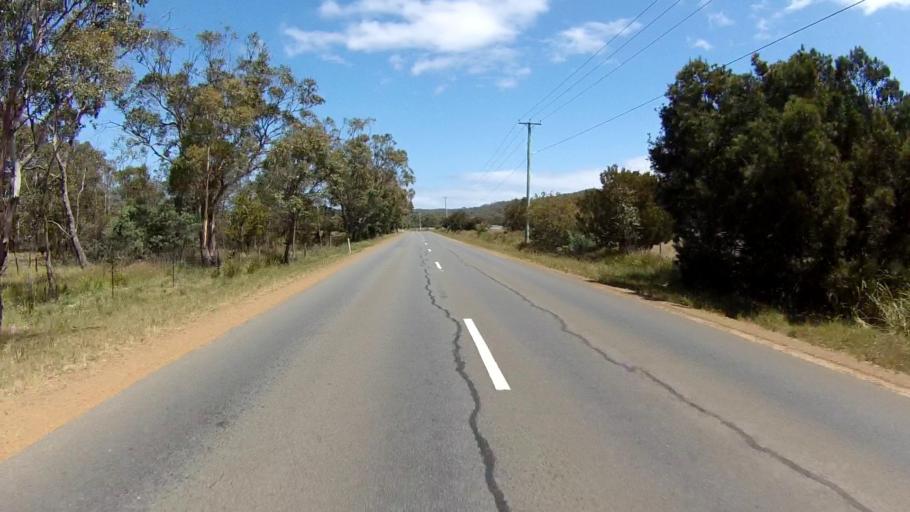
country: AU
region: Tasmania
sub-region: Clarence
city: Sandford
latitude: -42.9424
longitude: 147.4863
